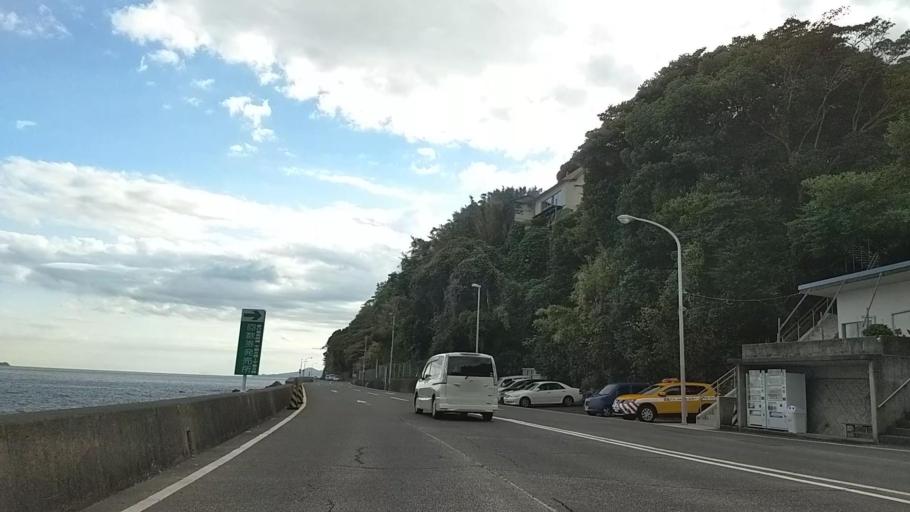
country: JP
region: Kanagawa
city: Yugawara
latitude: 35.1379
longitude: 139.1094
